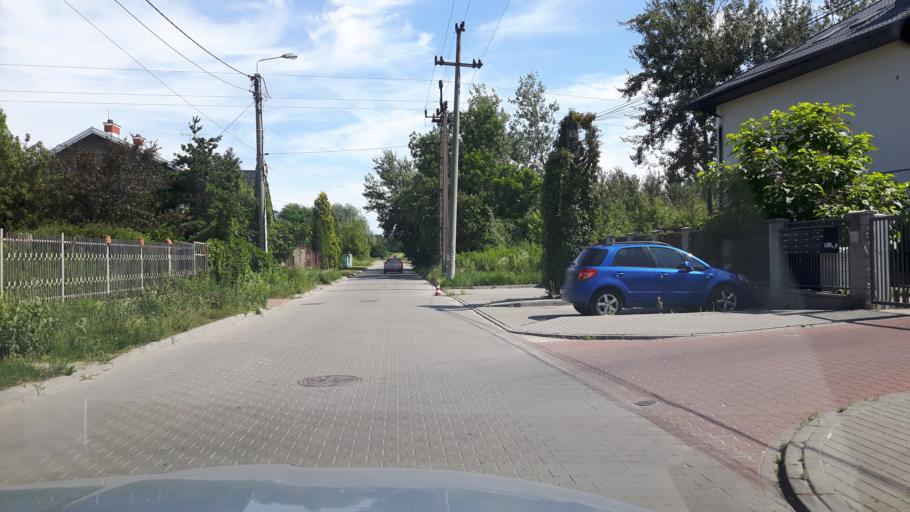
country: PL
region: Masovian Voivodeship
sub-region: Powiat wolominski
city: Marki
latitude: 52.3131
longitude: 21.1138
